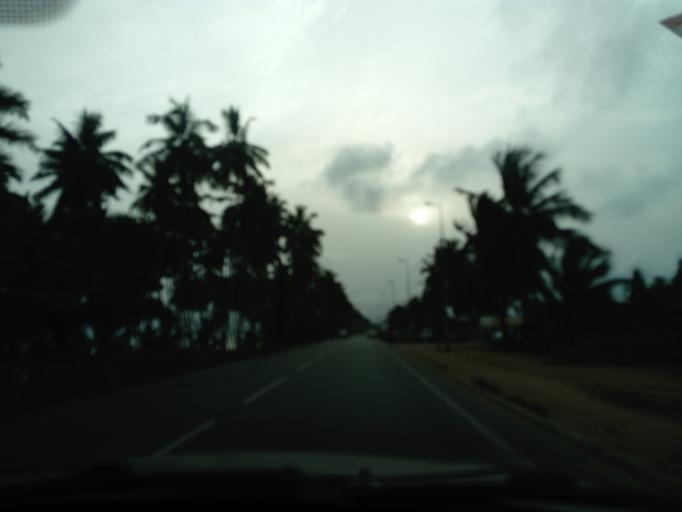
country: GH
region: Central
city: Cape Coast
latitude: 5.1009
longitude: -1.2792
